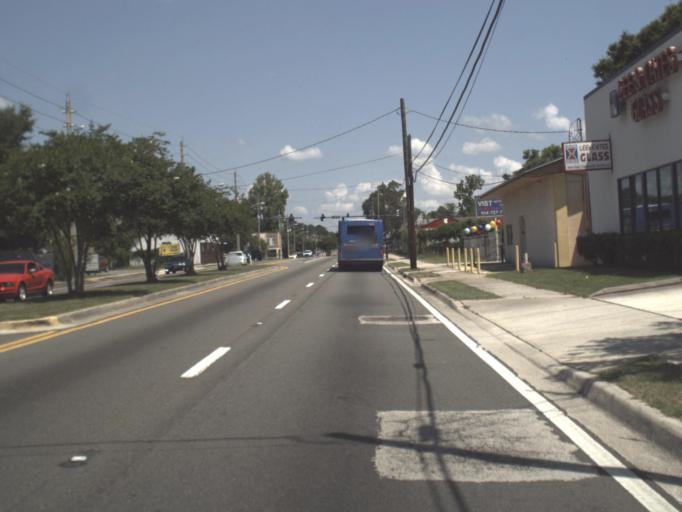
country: US
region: Florida
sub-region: Duval County
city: Jacksonville
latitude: 30.4051
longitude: -81.6858
